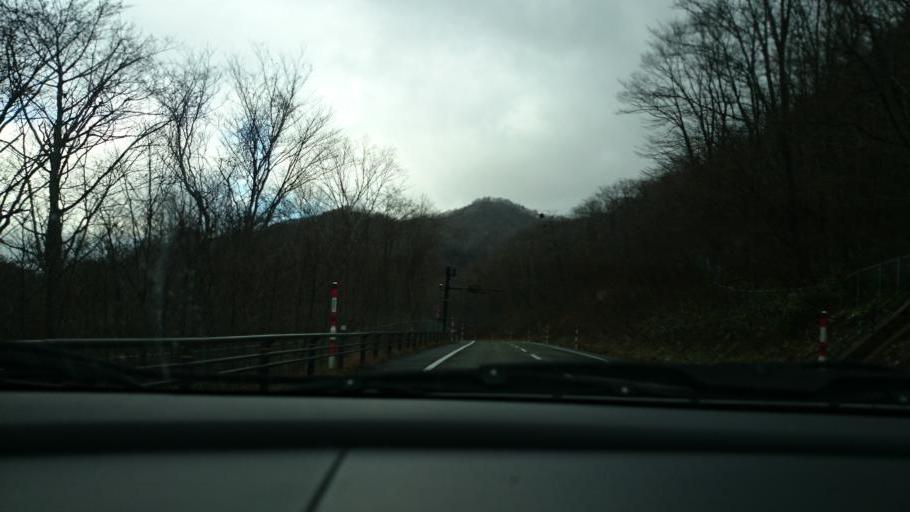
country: JP
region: Tochigi
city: Kuroiso
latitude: 37.2034
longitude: 139.9469
